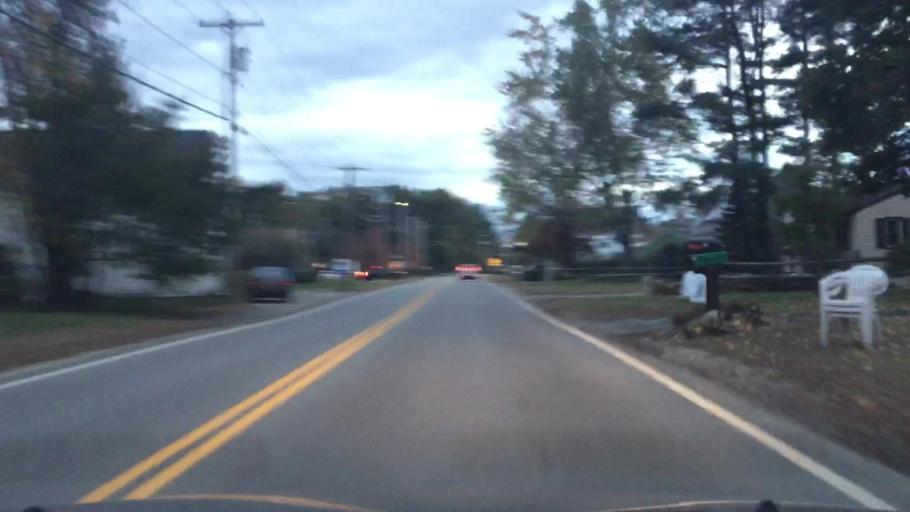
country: US
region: New Hampshire
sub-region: Cheshire County
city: Keene
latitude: 42.9069
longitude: -72.2649
